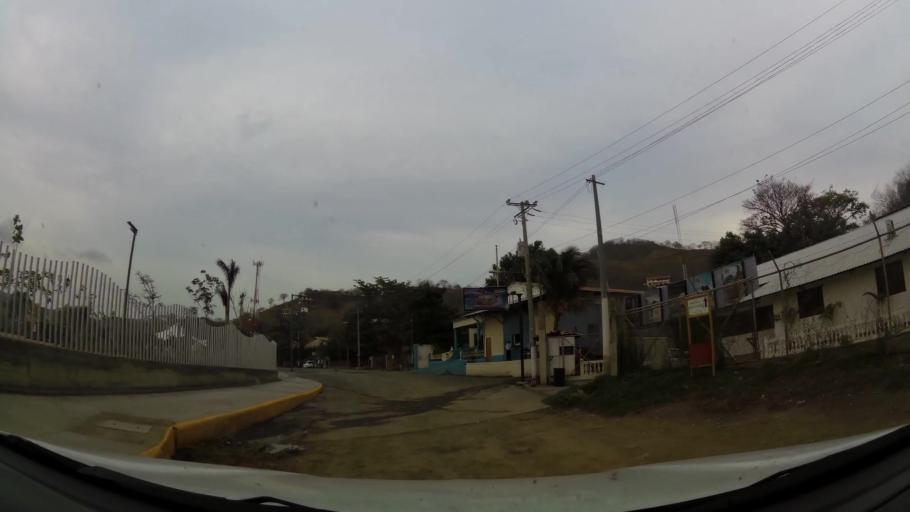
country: NI
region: Rivas
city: San Juan del Sur
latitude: 11.2497
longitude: -85.8749
